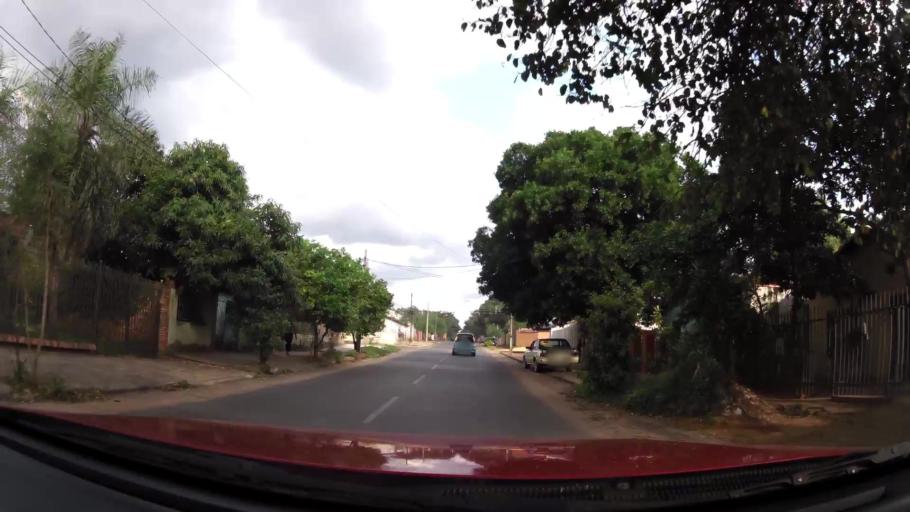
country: PY
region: Central
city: Fernando de la Mora
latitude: -25.3387
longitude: -57.5622
